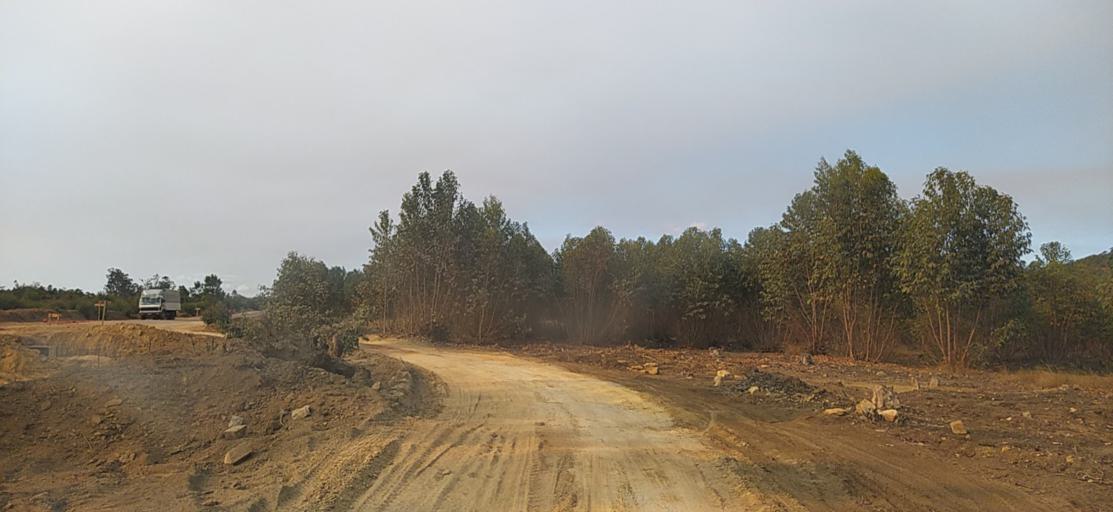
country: MG
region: Alaotra Mangoro
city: Moramanga
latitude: -18.6191
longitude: 48.2767
